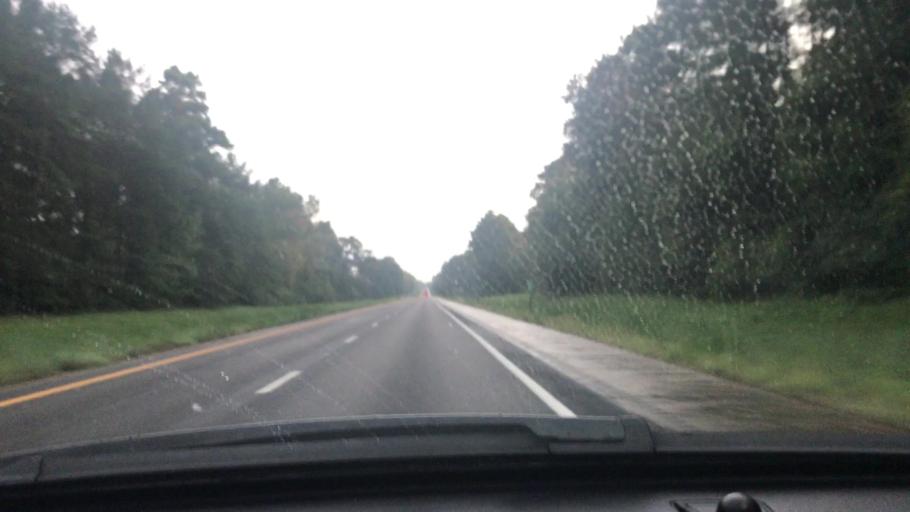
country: US
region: Mississippi
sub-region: Pike County
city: Magnolia
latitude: 31.0864
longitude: -90.4898
